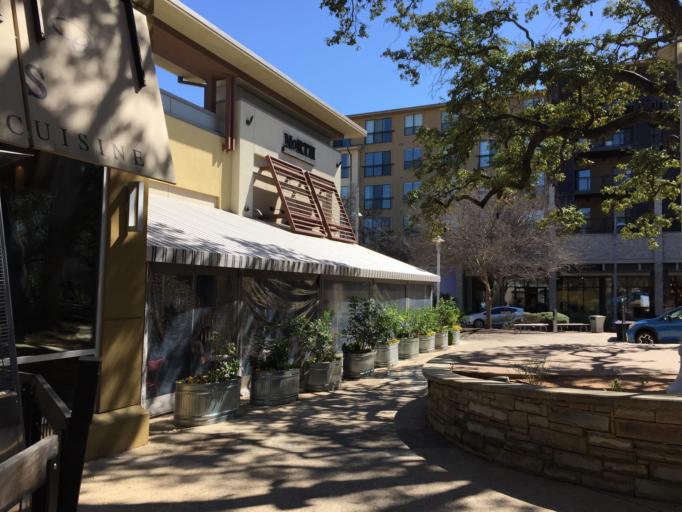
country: US
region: Texas
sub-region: Williamson County
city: Jollyville
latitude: 30.4023
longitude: -97.7263
